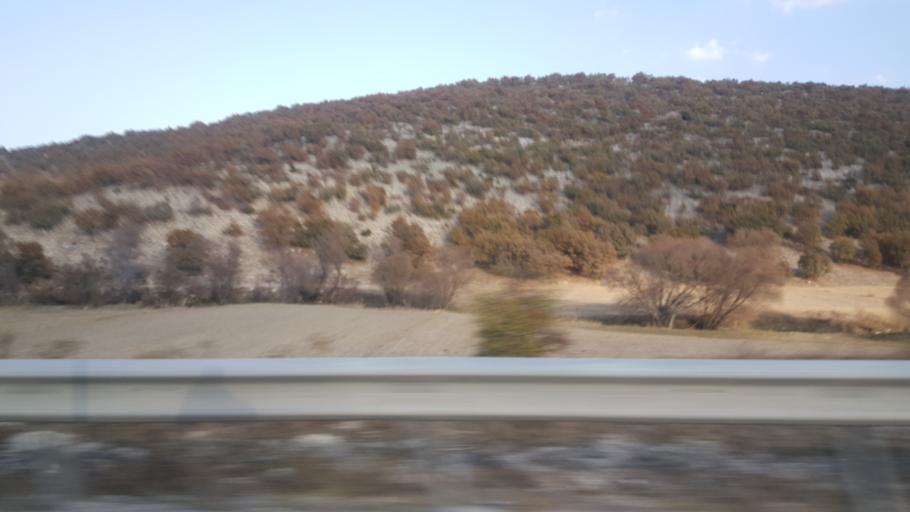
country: TR
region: Eskisehir
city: Kirka
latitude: 39.3491
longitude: 30.5875
